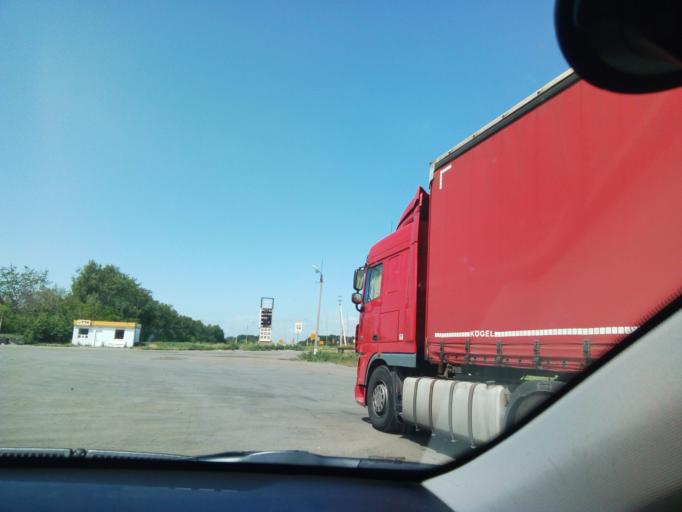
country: RU
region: Lipetsk
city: Gryazi
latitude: 52.5679
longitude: 40.1313
